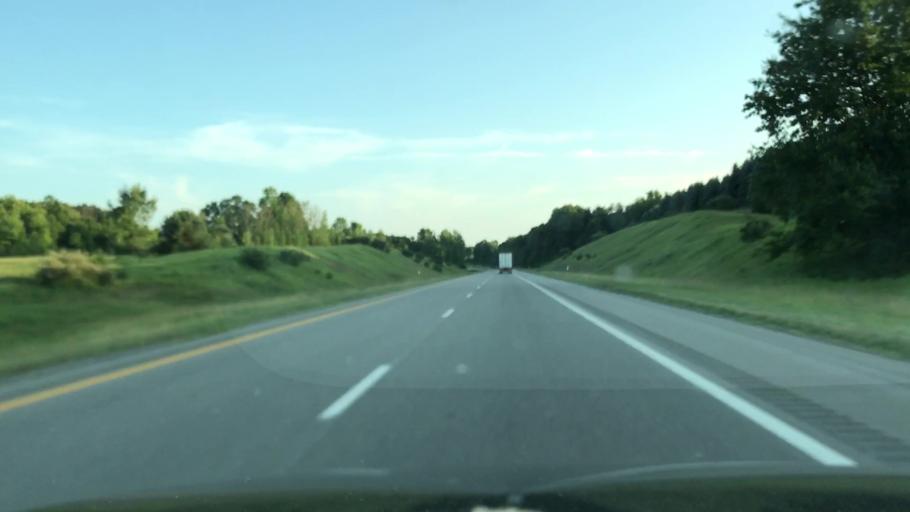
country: US
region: Michigan
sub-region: Osceola County
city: Reed City
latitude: 43.8705
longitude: -85.5324
